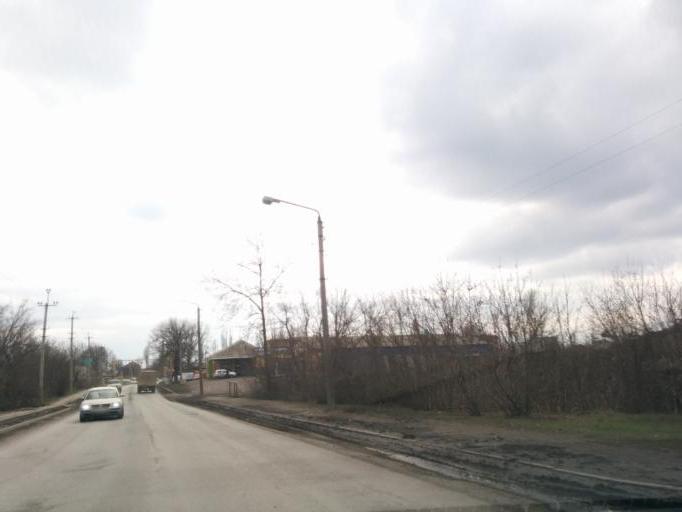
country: RU
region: Rostov
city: Shakhty
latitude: 47.6915
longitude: 40.2582
